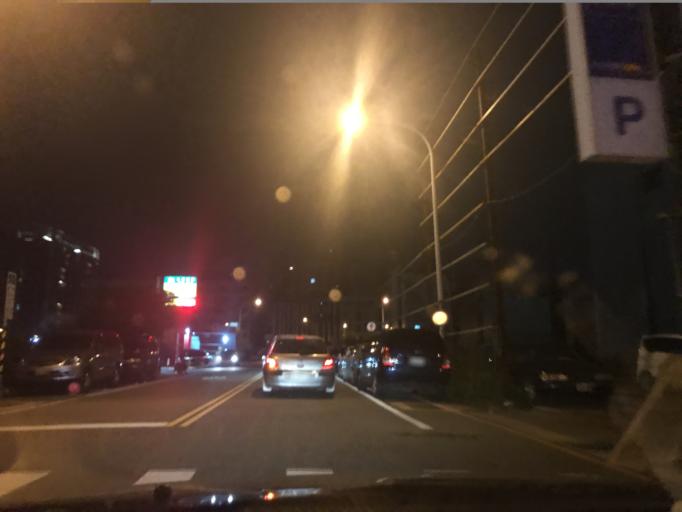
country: TW
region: Taiwan
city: Daxi
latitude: 24.9331
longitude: 121.2834
